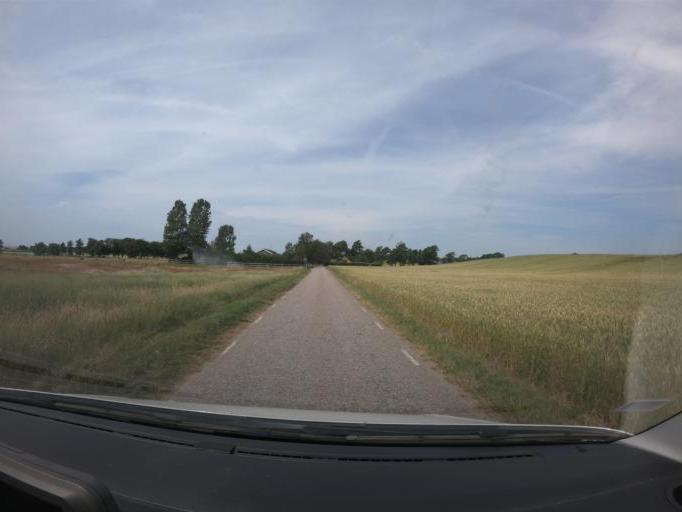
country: SE
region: Skane
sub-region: Angelholms Kommun
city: Vejbystrand
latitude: 56.3655
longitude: 12.7367
